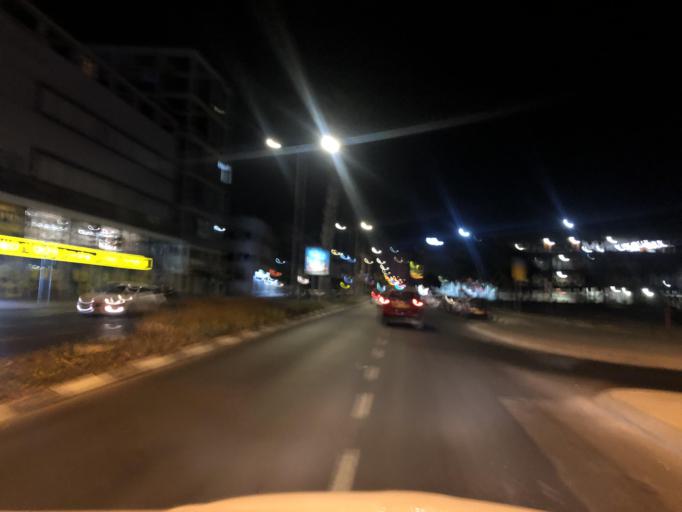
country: IL
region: Tel Aviv
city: Yafo
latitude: 32.0527
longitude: 34.7656
